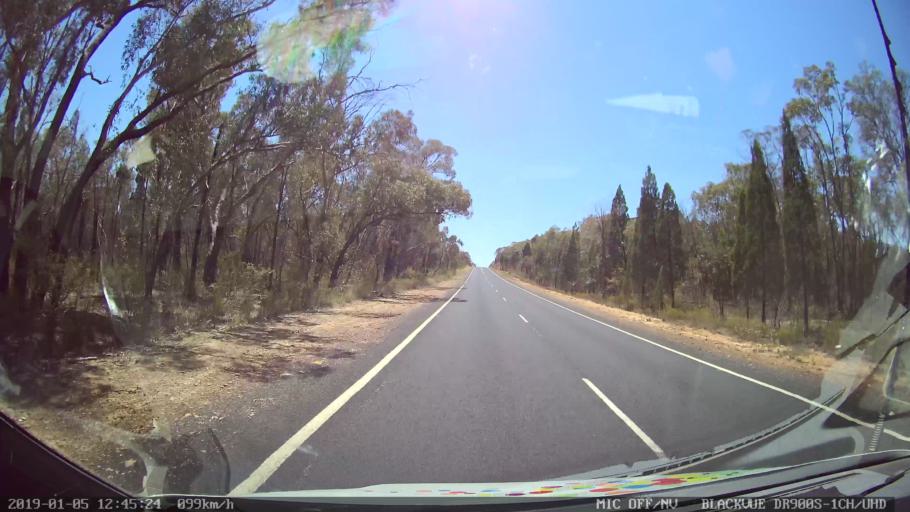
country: AU
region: New South Wales
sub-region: Warrumbungle Shire
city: Coonabarabran
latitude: -31.1282
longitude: 149.5495
